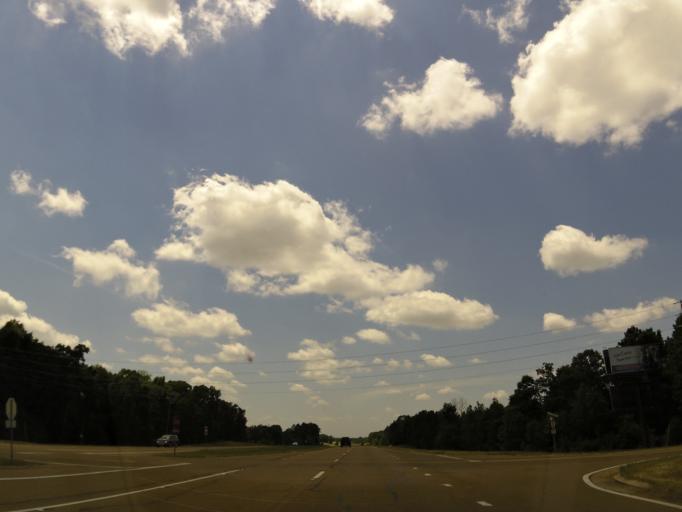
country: US
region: Mississippi
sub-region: Pontotoc County
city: Pontotoc
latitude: 34.2833
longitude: -89.0710
